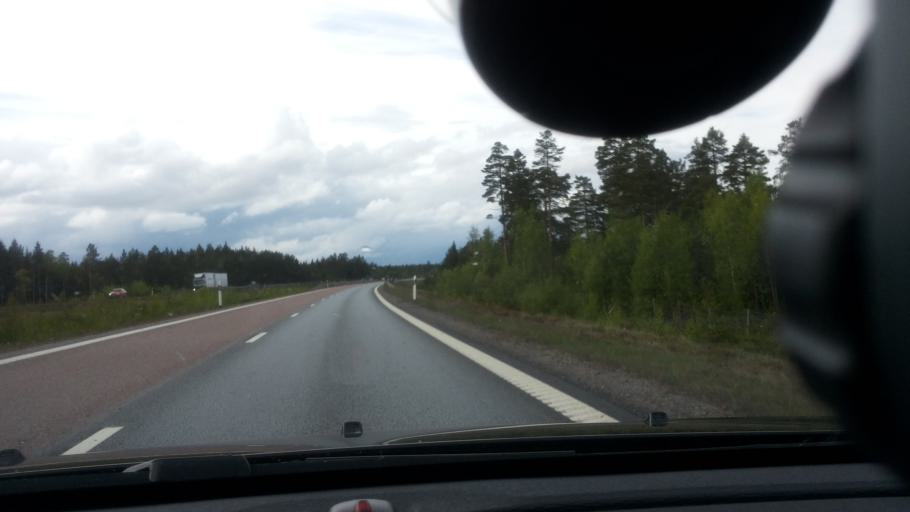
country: SE
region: Gaevleborg
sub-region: Soderhamns Kommun
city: Soderhamn
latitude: 61.3782
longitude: 16.9955
